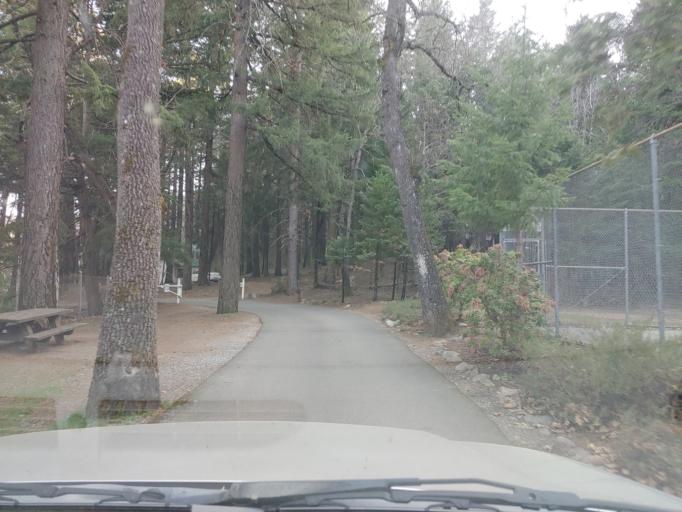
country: US
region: California
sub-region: Siskiyou County
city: Dunsmuir
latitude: 41.2254
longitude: -122.2775
